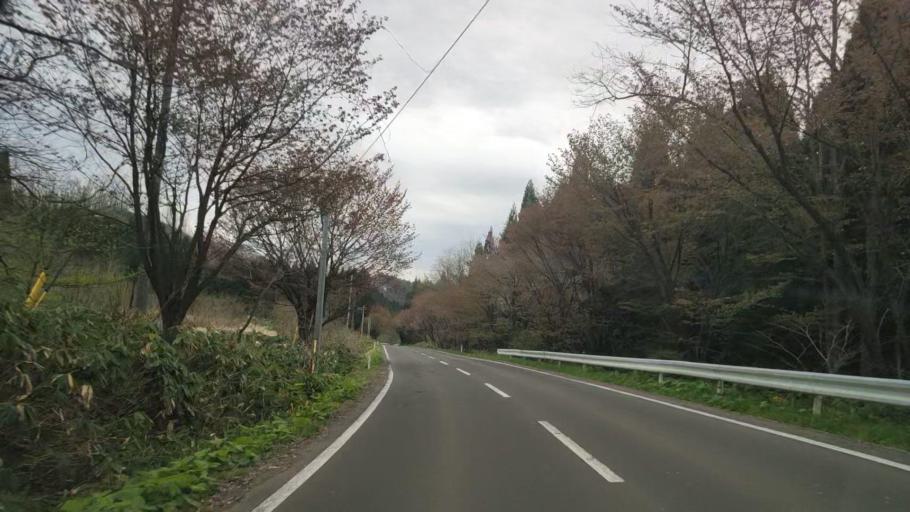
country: JP
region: Akita
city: Hanawa
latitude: 40.3495
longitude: 140.7749
